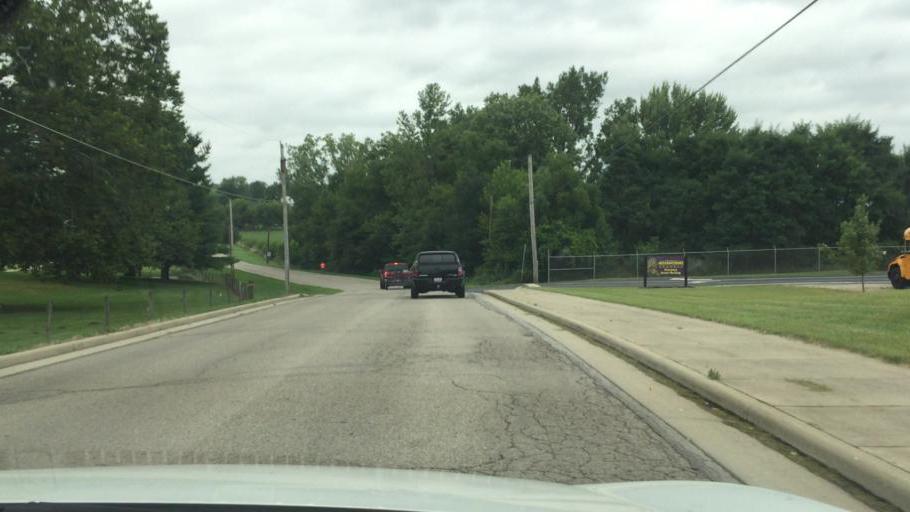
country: US
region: Ohio
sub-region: Champaign County
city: Mechanicsburg
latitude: 40.0775
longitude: -83.5635
